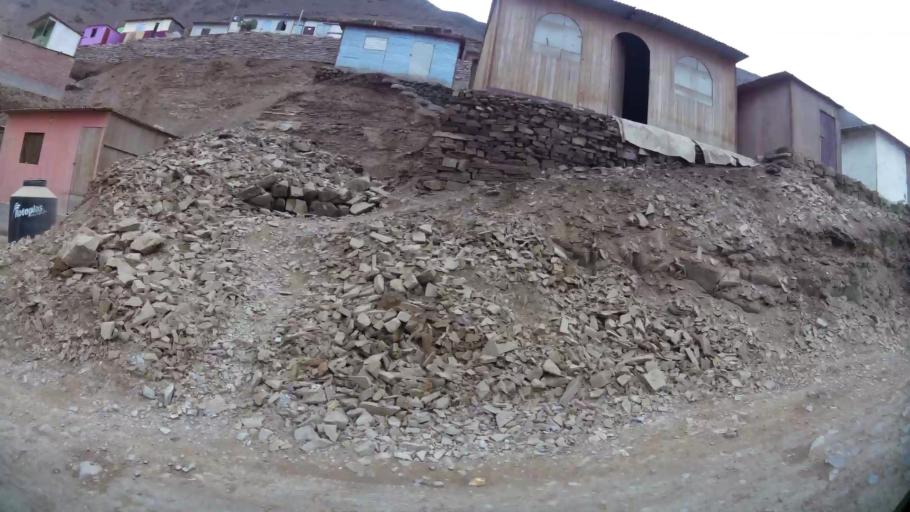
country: PE
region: Lima
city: Ventanilla
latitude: -11.9136
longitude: -77.0923
